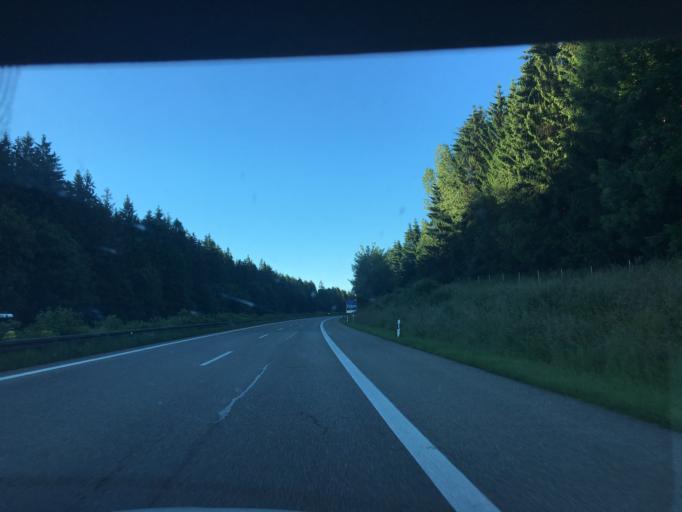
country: DE
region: Bavaria
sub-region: Swabia
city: Wolfertschwenden
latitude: 47.8619
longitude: 10.2748
